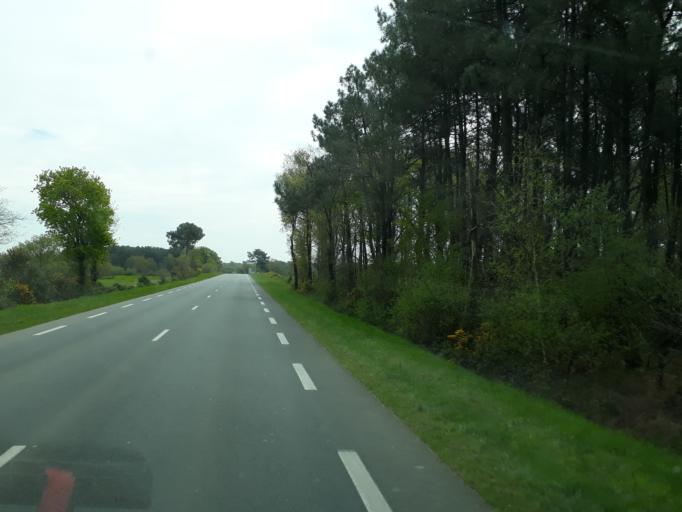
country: FR
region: Brittany
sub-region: Departement du Morbihan
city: Peaule
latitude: 47.5292
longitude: -2.3866
